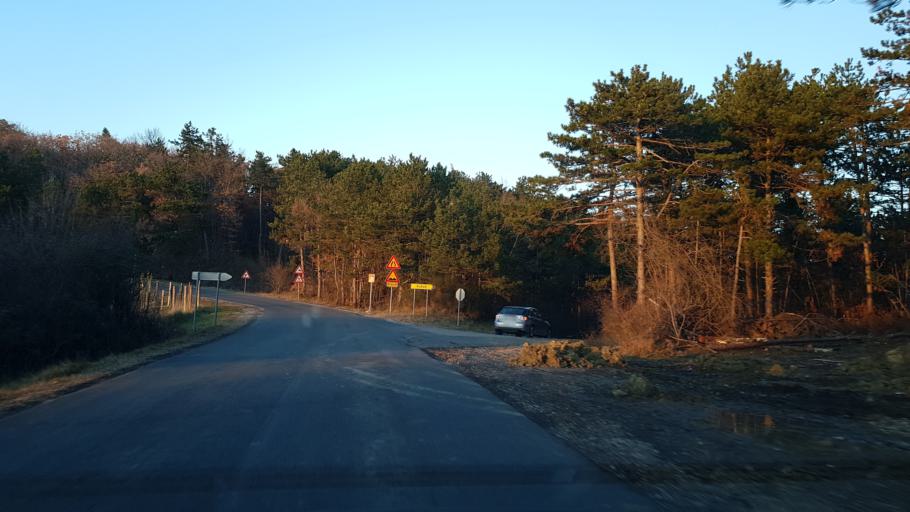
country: SI
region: Koper-Capodistria
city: Sv. Anton
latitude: 45.5176
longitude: 13.8597
